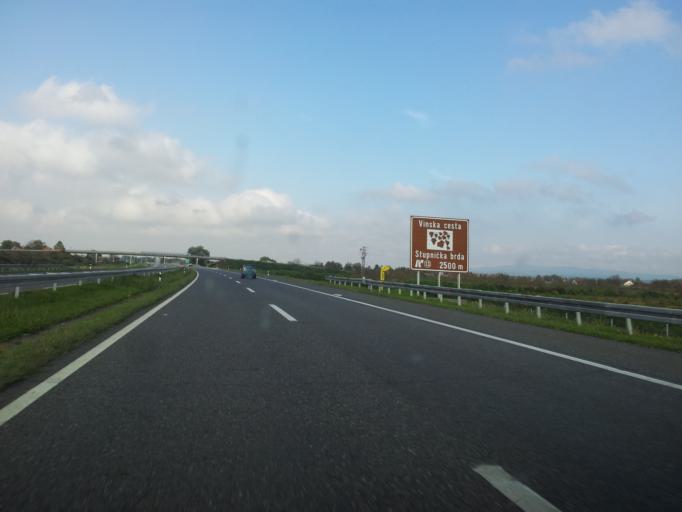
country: HR
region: Brodsko-Posavska
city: Luzani
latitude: 45.1620
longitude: 17.7127
